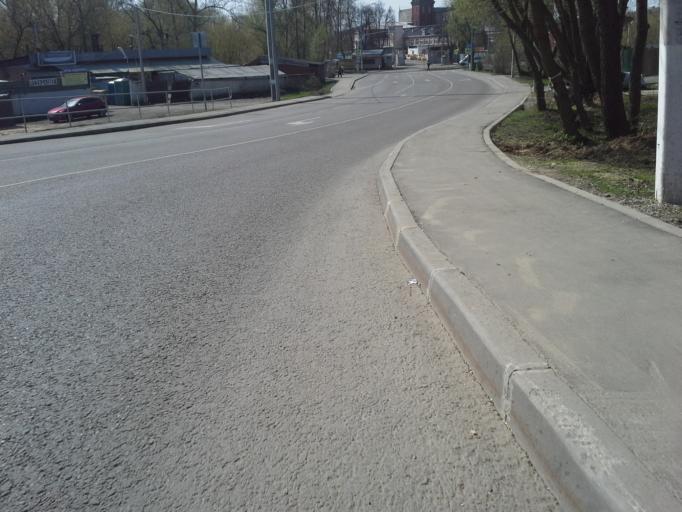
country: RU
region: Moskovskaya
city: Dubrovitsy
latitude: 55.4896
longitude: 37.5059
